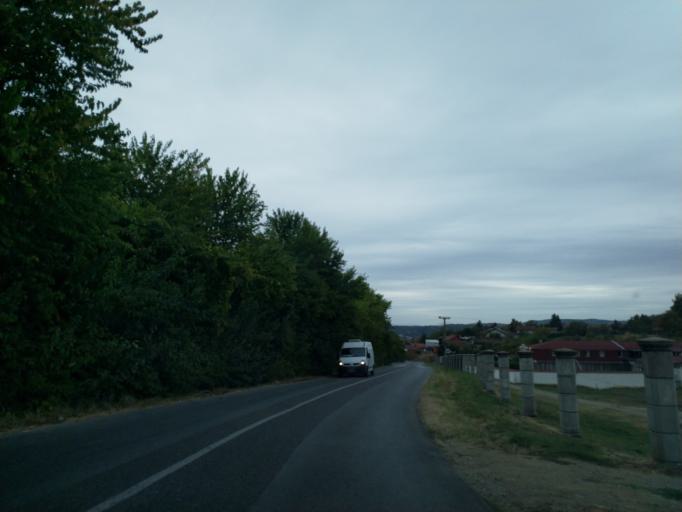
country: RS
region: Central Serbia
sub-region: Pomoravski Okrug
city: Jagodina
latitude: 43.9914
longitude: 21.2305
